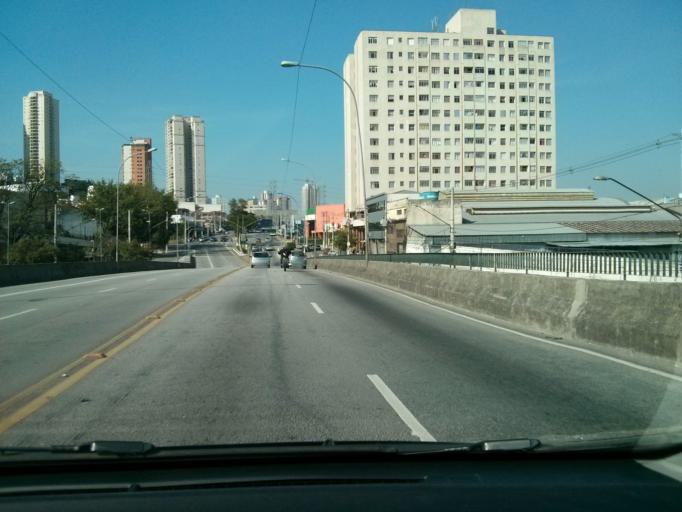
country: BR
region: Sao Paulo
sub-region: Sao Paulo
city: Sao Paulo
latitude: -23.5817
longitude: -46.5949
